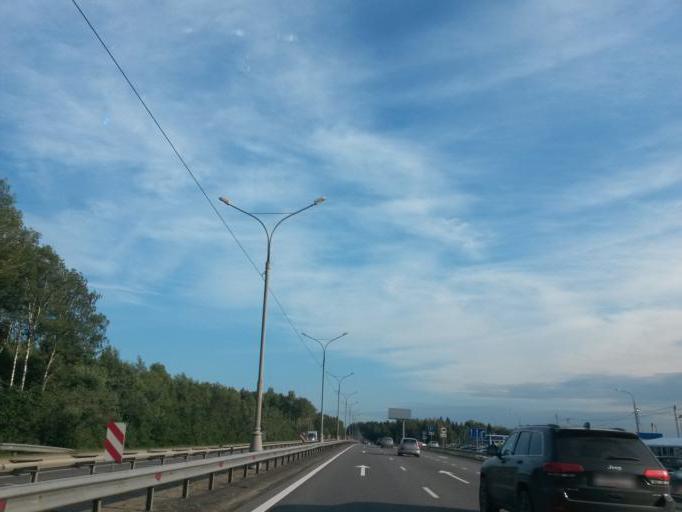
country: RU
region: Moskovskaya
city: Vostryakovo
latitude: 55.4672
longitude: 37.8536
